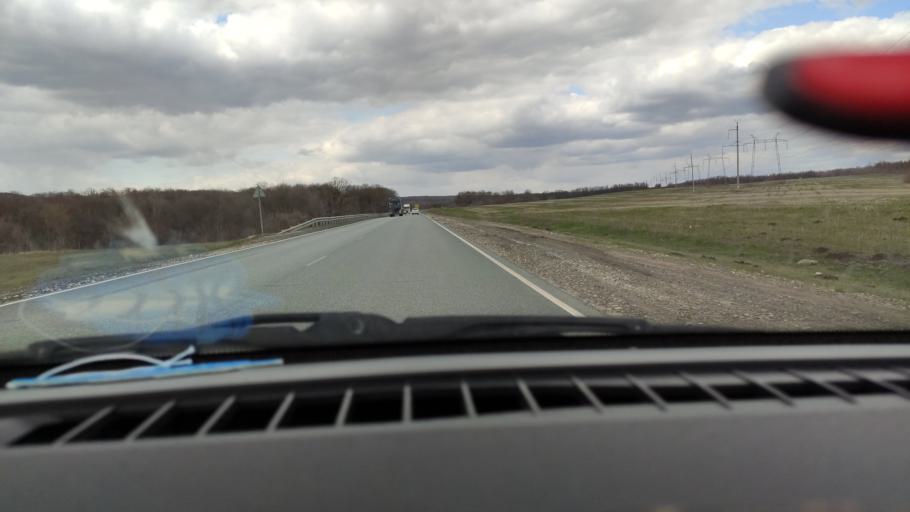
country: RU
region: Saratov
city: Tersa
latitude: 52.1018
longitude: 47.4643
